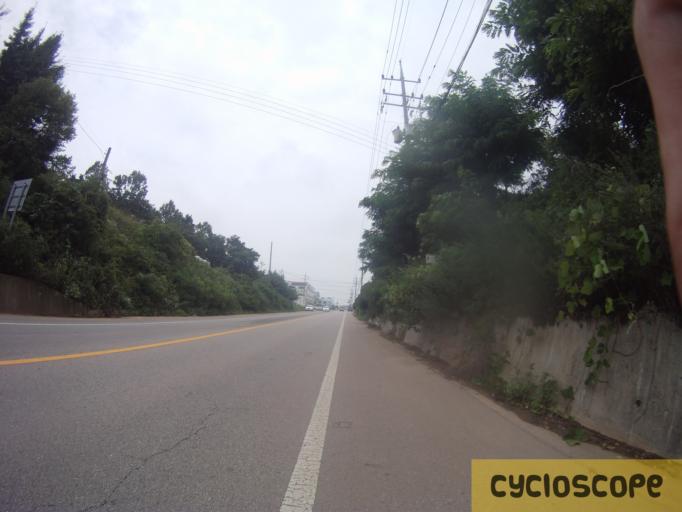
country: KR
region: Gyeonggi-do
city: Hwaseong-si
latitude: 37.1541
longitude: 126.8840
